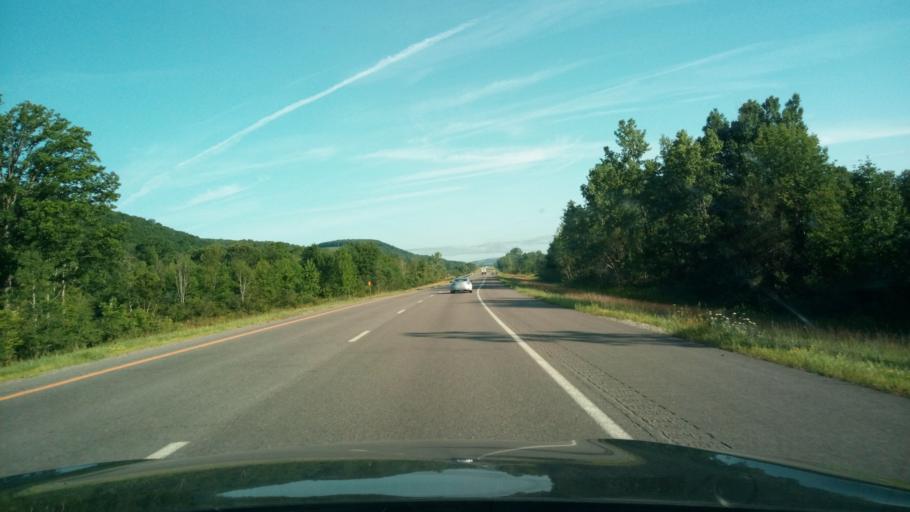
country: US
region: New York
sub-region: Steuben County
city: Wayland
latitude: 42.4463
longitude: -77.4720
